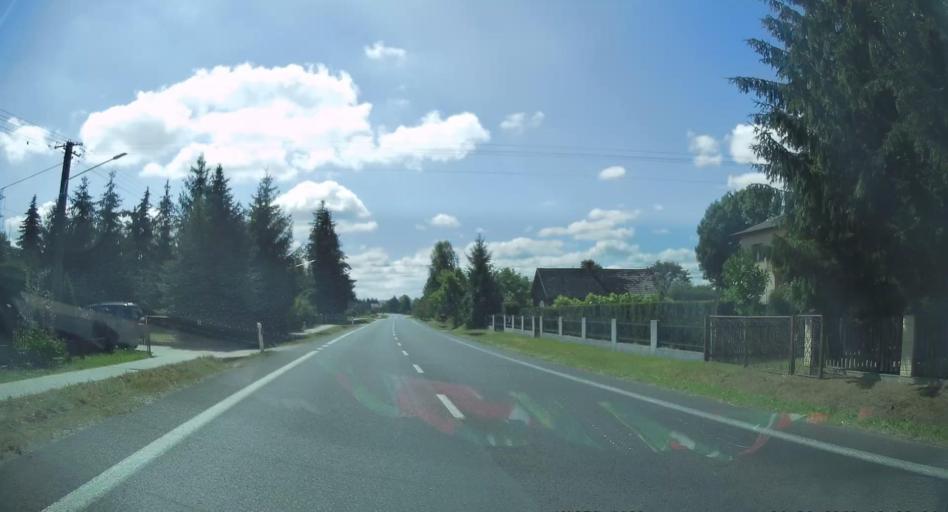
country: PL
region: Subcarpathian Voivodeship
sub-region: Powiat debicki
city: Brzeznica
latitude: 50.1313
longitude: 21.4856
